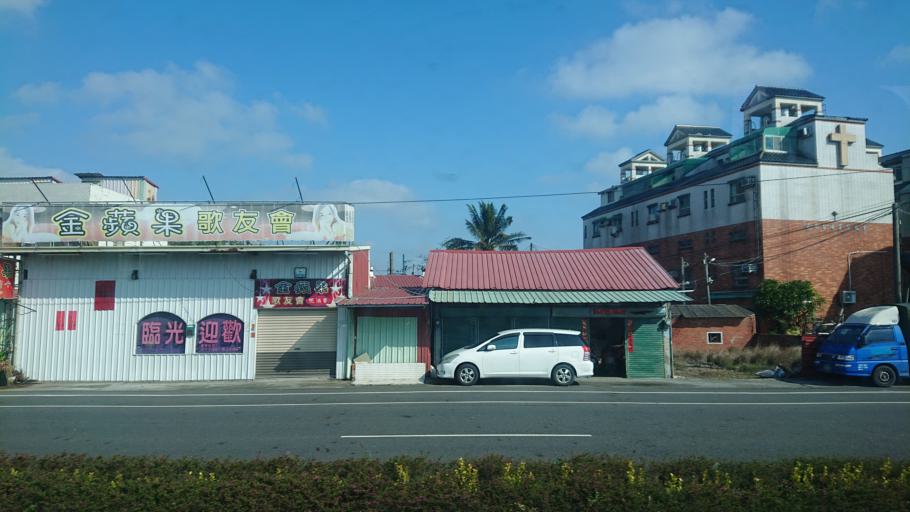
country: TW
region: Taiwan
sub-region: Chiayi
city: Taibao
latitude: 23.4578
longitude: 120.3086
